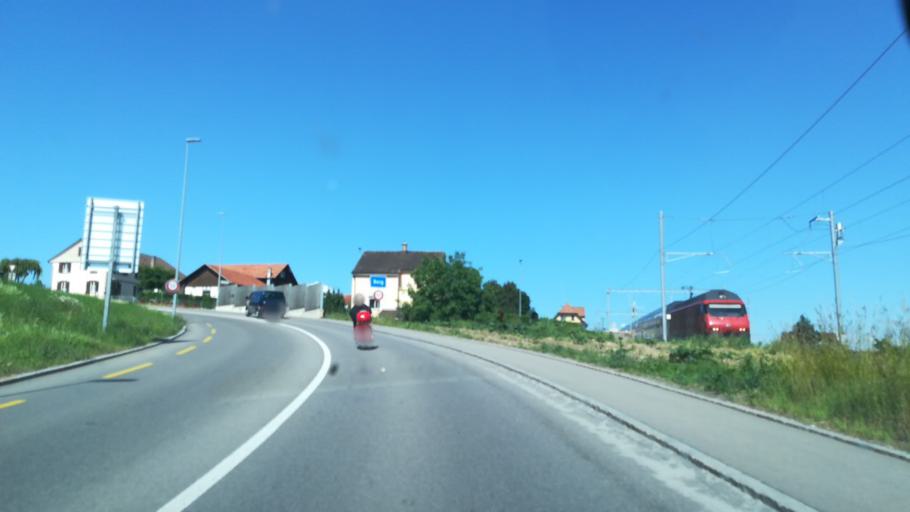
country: CH
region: Thurgau
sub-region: Weinfelden District
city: Berg
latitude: 47.5719
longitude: 9.1674
